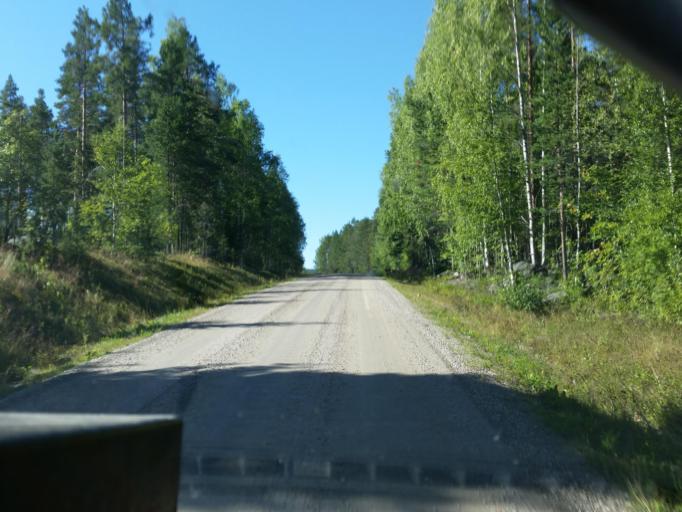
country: SE
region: Norrbotten
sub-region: Pitea Kommun
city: Roknas
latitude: 65.3419
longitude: 21.1321
